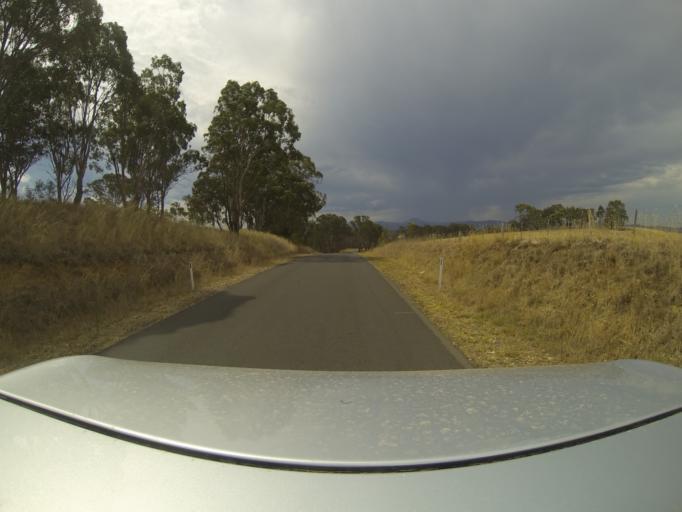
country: AU
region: Victoria
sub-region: Wellington
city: Heyfield
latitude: -37.9039
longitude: 146.7225
